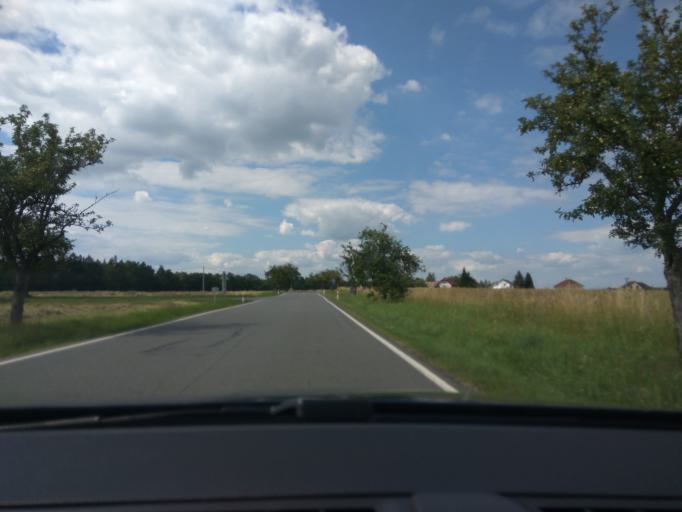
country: CZ
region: Jihocesky
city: Milevsko
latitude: 49.4111
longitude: 14.3594
